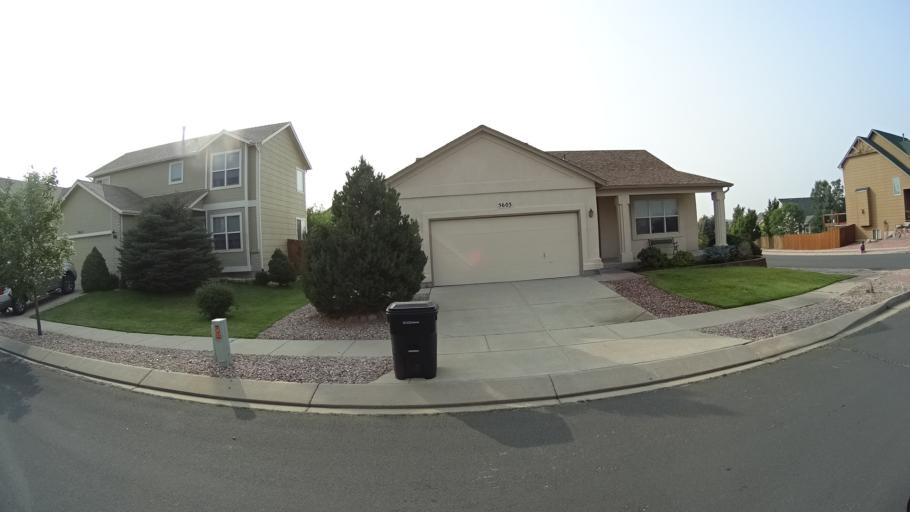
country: US
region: Colorado
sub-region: El Paso County
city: Cimarron Hills
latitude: 38.9320
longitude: -104.7241
